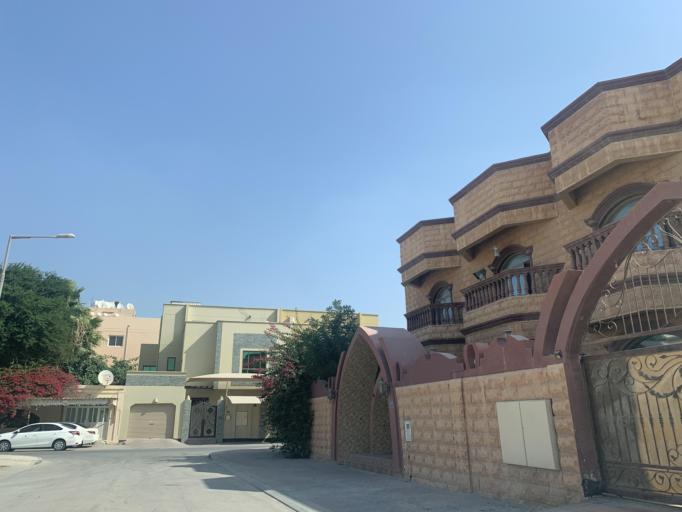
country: BH
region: Central Governorate
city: Madinat Hamad
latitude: 26.1388
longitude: 50.4936
